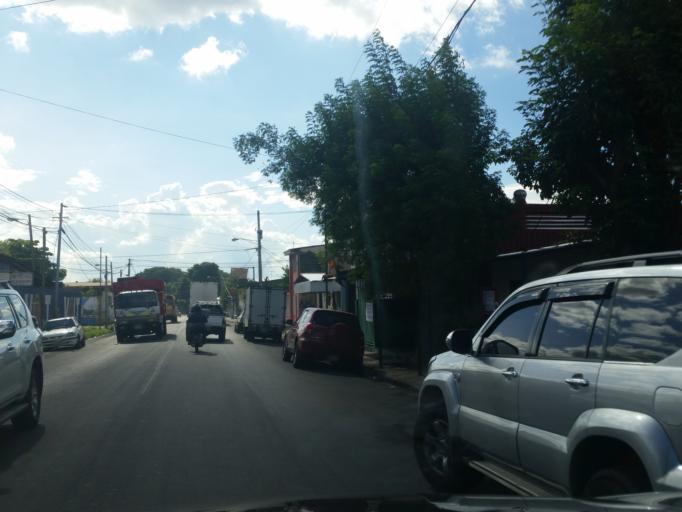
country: NI
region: Managua
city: Managua
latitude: 12.1557
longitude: -86.2880
